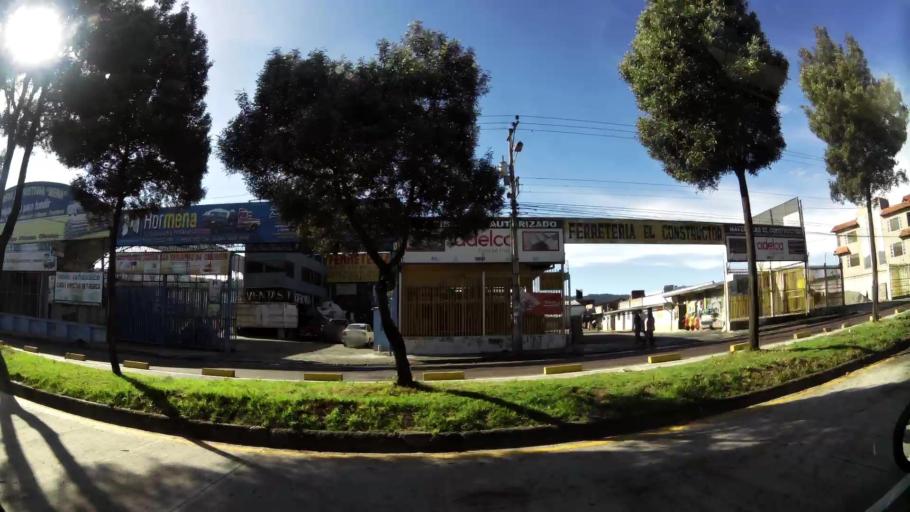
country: EC
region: Pichincha
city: Quito
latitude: -0.3084
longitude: -78.5449
